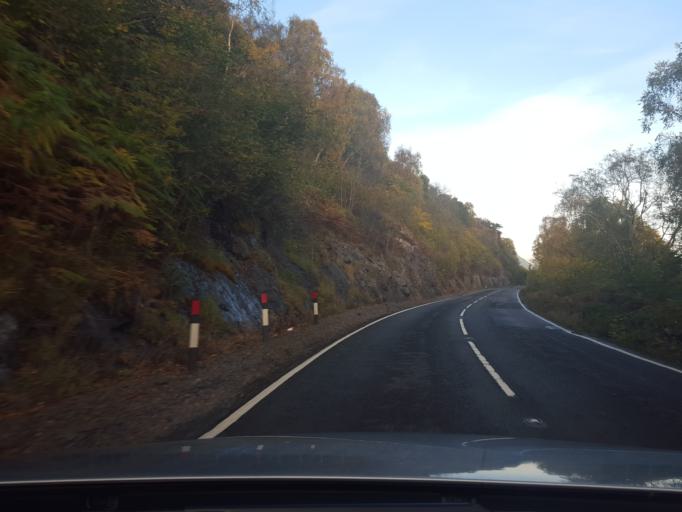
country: GB
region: Scotland
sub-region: Highland
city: Beauly
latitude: 57.3679
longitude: -4.3894
